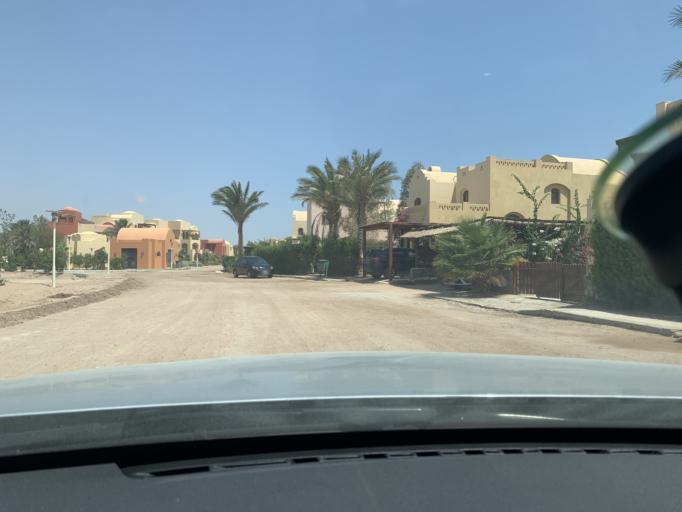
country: EG
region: Red Sea
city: El Gouna
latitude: 27.4035
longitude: 33.6705
